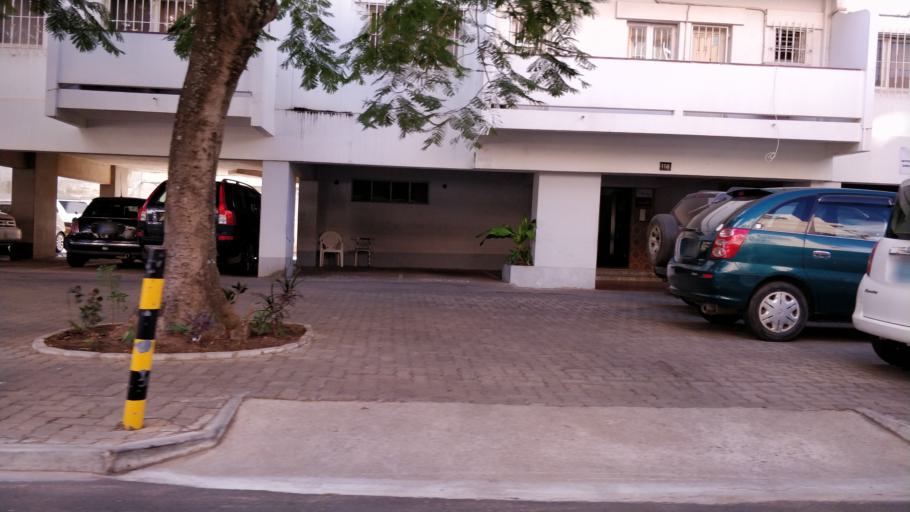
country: MZ
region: Maputo City
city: Maputo
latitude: -25.9720
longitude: 32.5936
